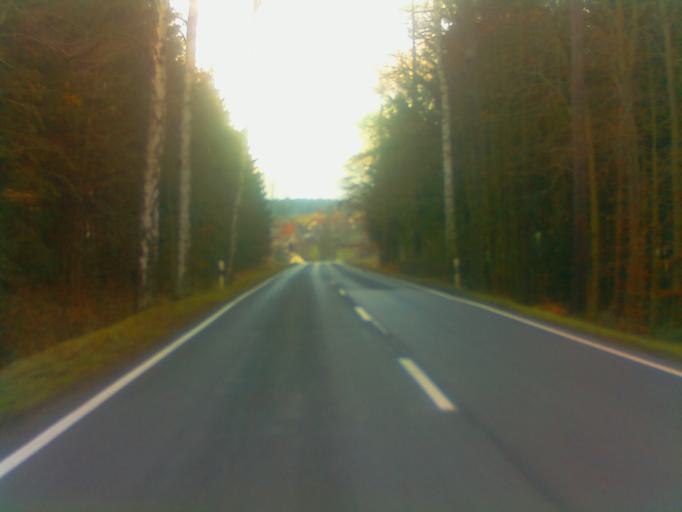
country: DE
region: Thuringia
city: Trockenborn-Wolfersdorf
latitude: 50.7544
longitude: 11.7044
